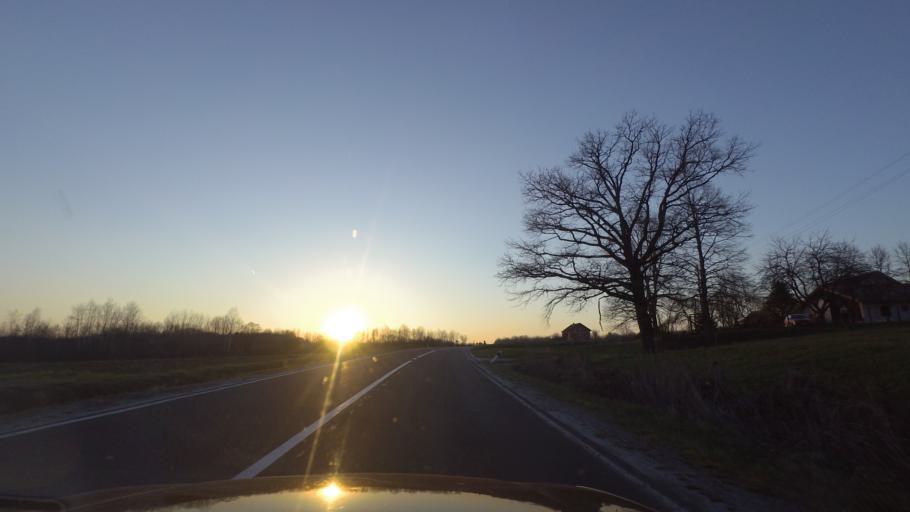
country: HR
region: Sisacko-Moslavacka
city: Gvozd
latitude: 45.3341
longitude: 15.9147
